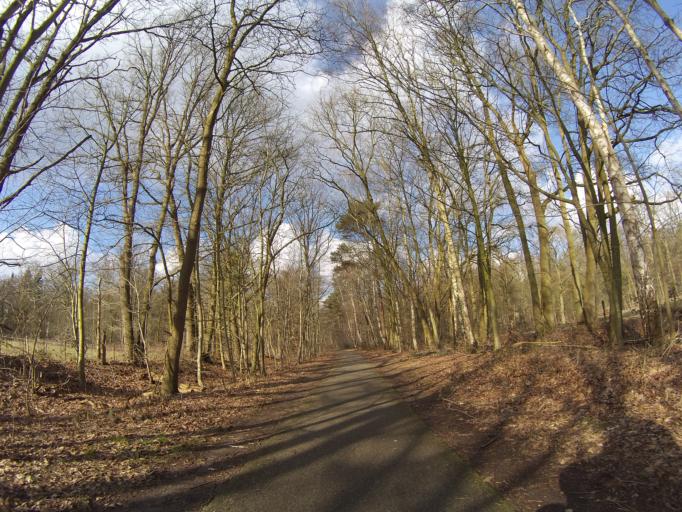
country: NL
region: Utrecht
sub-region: Gemeente Zeist
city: Zeist
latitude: 52.1134
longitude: 5.2513
